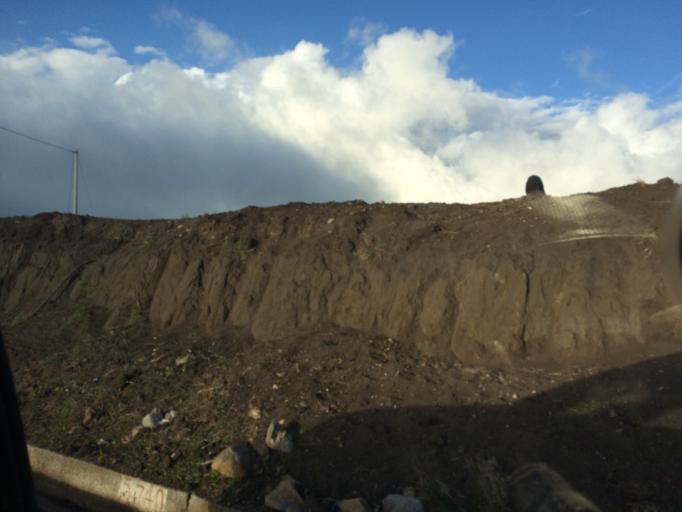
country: EC
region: Chimborazo
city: Alausi
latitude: -2.1321
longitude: -78.7192
